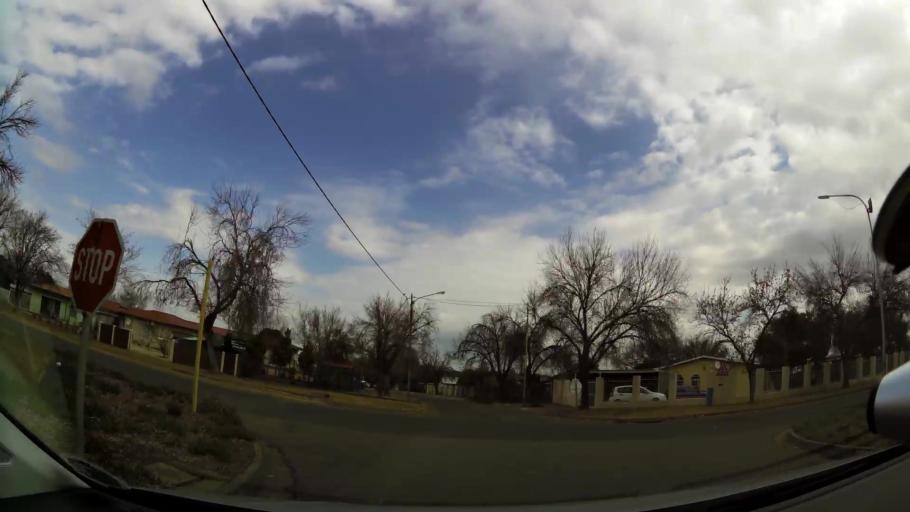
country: ZA
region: Orange Free State
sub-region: Fezile Dabi District Municipality
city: Kroonstad
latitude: -27.6405
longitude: 27.2291
